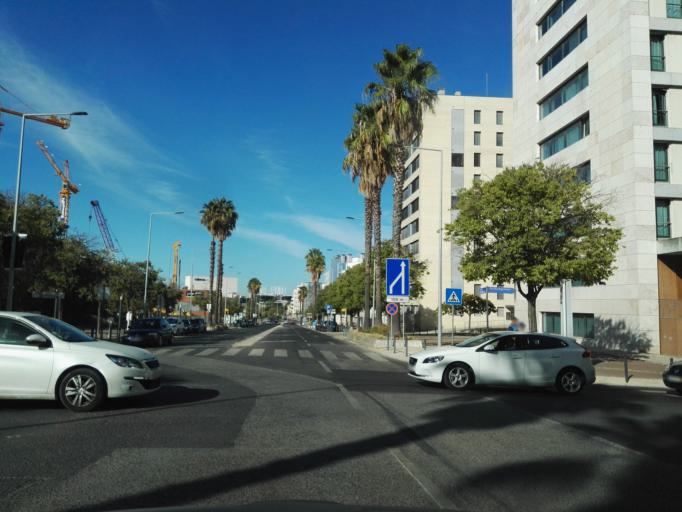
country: PT
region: Lisbon
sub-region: Loures
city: Moscavide
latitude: 38.7566
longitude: -9.0985
